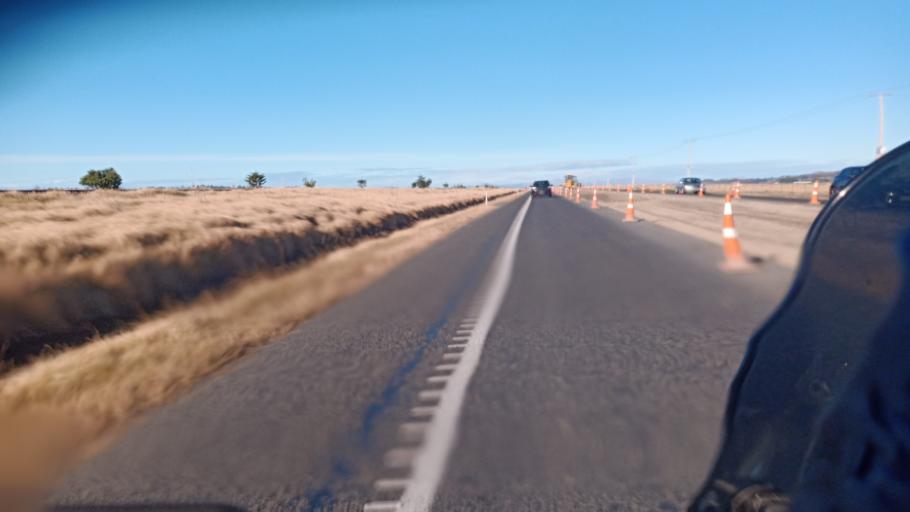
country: NZ
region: Hawke's Bay
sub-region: Napier City
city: Napier
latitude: -39.4476
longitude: 176.8714
